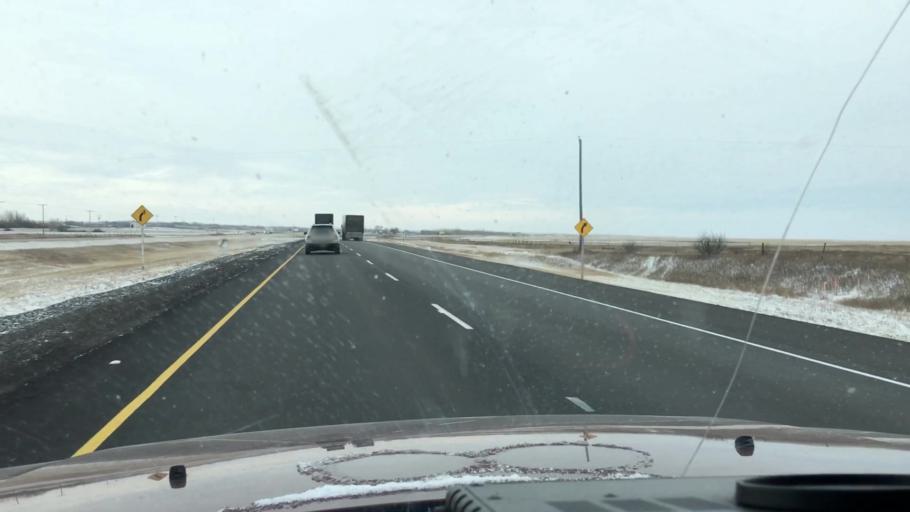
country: CA
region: Saskatchewan
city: Saskatoon
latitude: 51.7850
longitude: -106.4800
